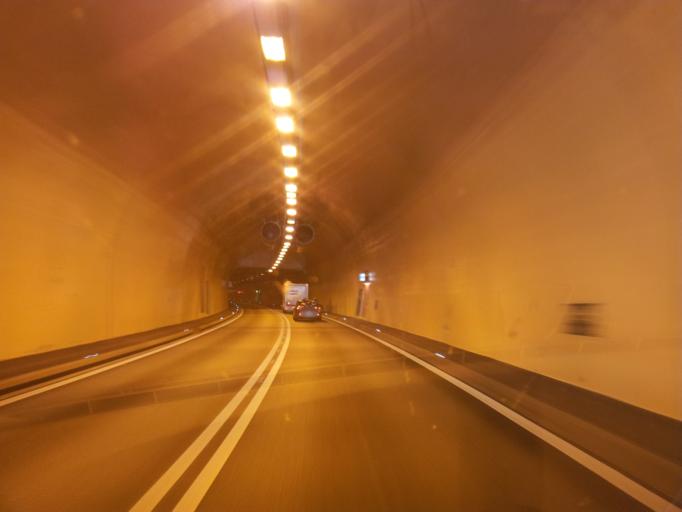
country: CH
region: Valais
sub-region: Visp District
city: Stalden
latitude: 46.2229
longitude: 7.8578
